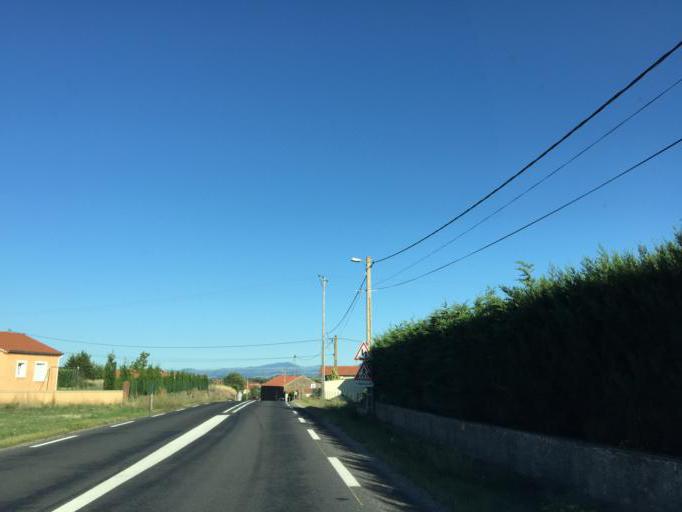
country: FR
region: Auvergne
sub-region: Departement de la Haute-Loire
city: Bains
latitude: 45.0095
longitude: 3.7968
